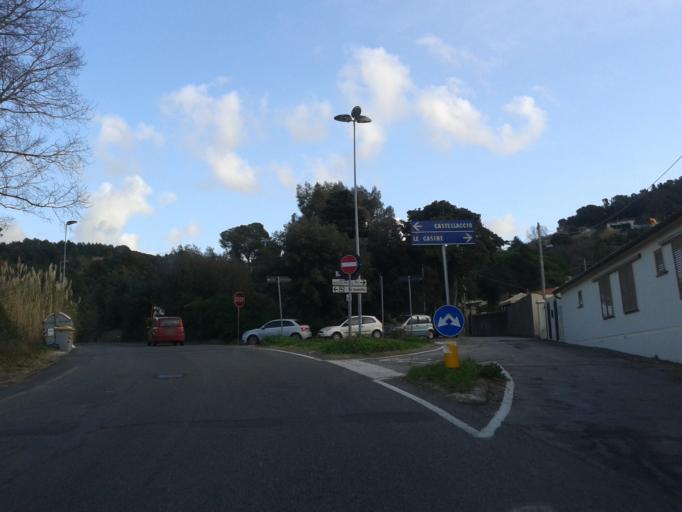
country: IT
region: Tuscany
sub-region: Provincia di Livorno
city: Quercianella
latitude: 43.4980
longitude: 10.3498
